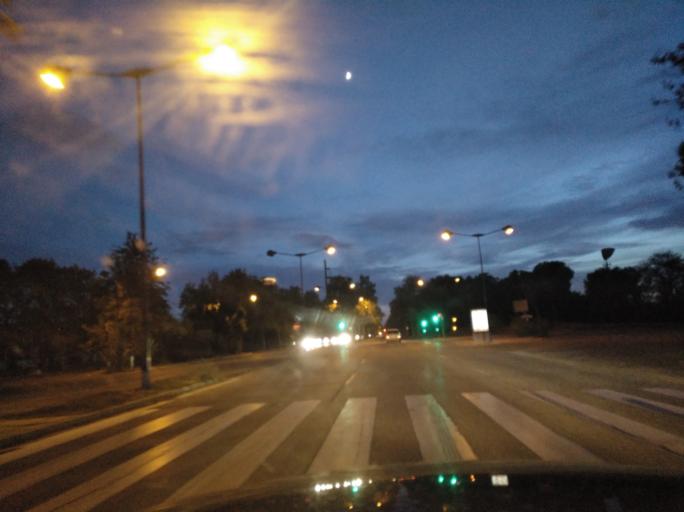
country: ES
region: Andalusia
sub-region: Provincia de Sevilla
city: Camas
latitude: 37.4043
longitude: -6.0104
